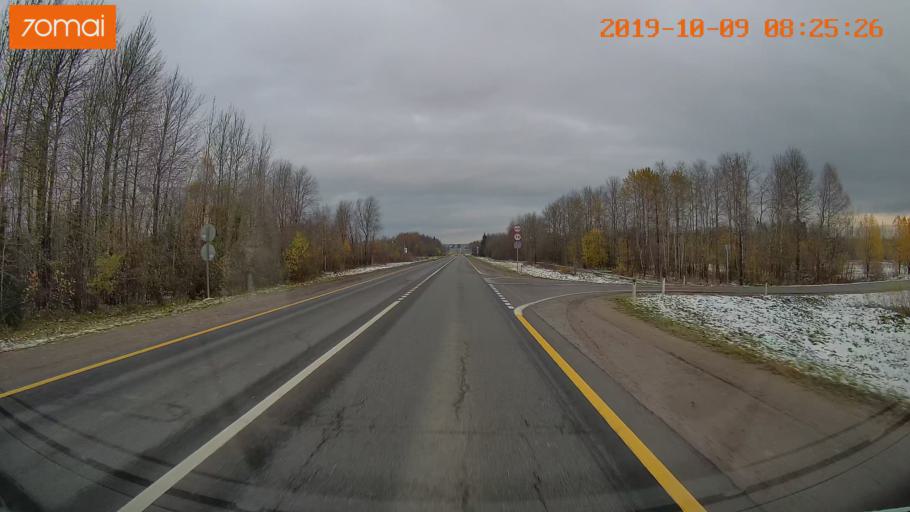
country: RU
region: Vologda
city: Gryazovets
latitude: 58.7812
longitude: 40.2723
